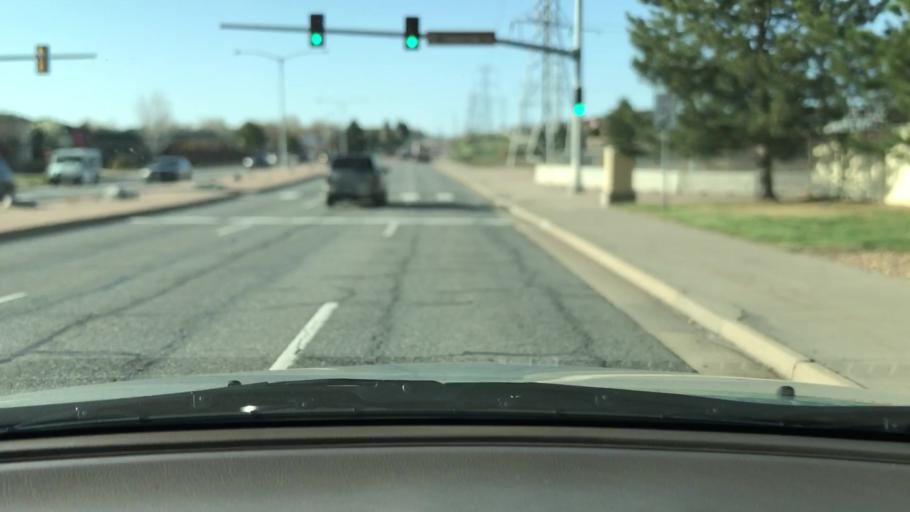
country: US
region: Colorado
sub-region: Adams County
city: Aurora
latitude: 39.6669
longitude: -104.7723
